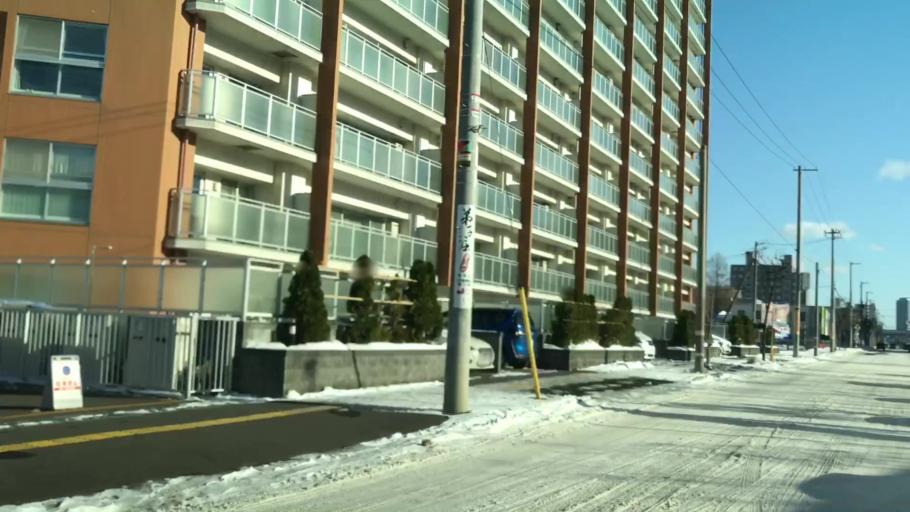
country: JP
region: Hokkaido
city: Sapporo
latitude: 43.0977
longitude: 141.2769
